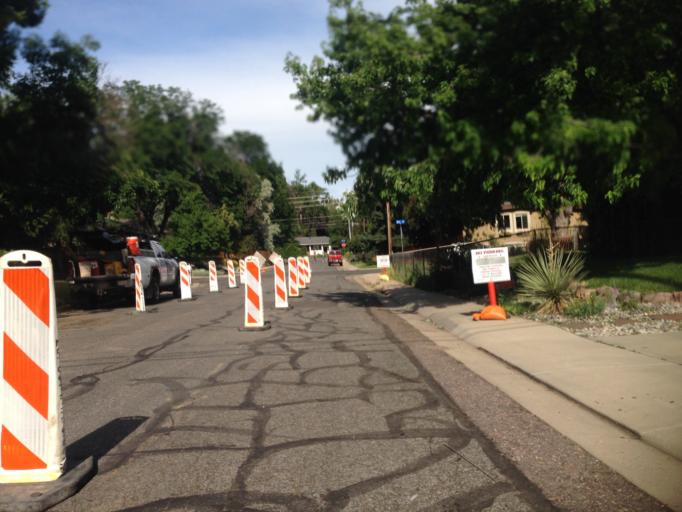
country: US
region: Colorado
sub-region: Boulder County
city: Boulder
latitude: 40.0280
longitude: -105.2744
